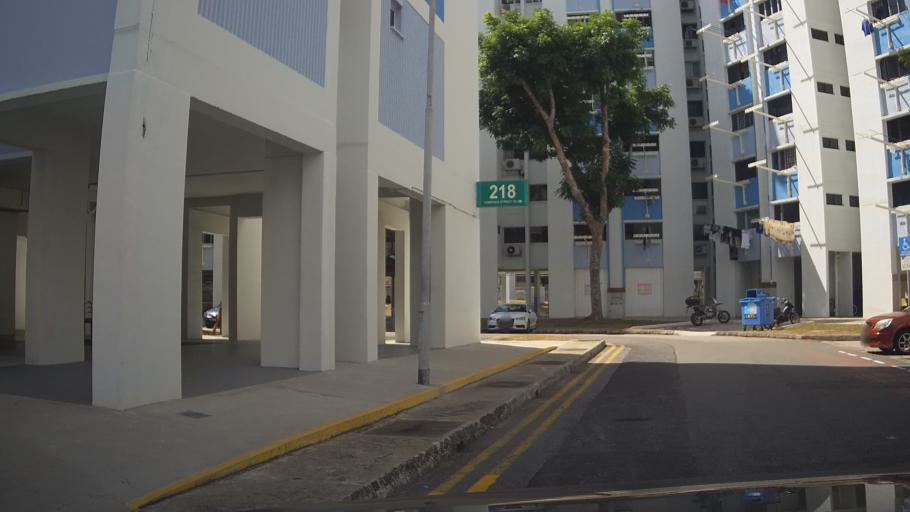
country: SG
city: Singapore
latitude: 1.3545
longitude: 103.9521
